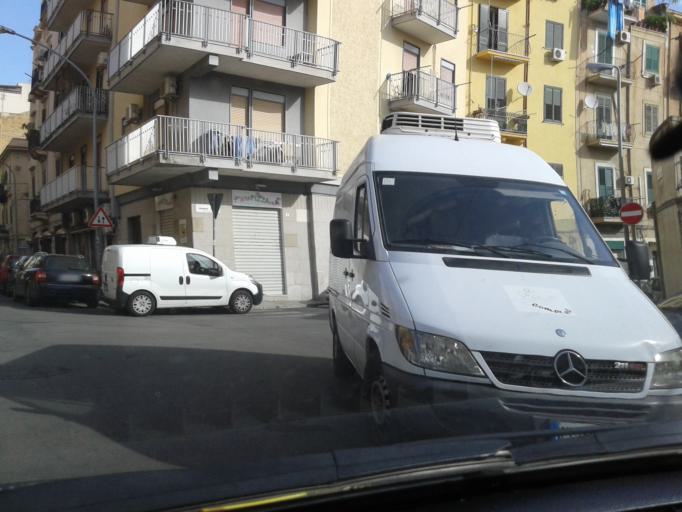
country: IT
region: Sicily
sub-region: Palermo
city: Palermo
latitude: 38.1046
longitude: 13.3399
